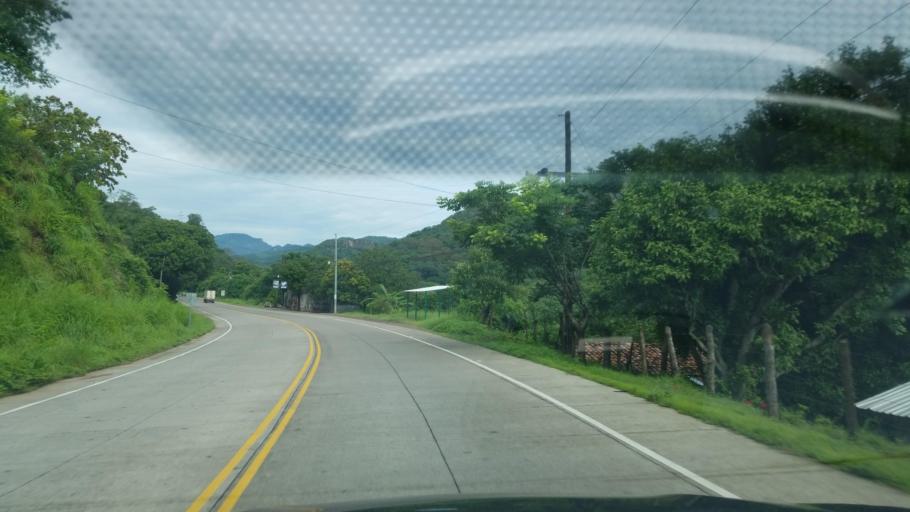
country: HN
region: Francisco Morazan
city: El Porvenir
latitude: 13.6864
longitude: -87.3433
